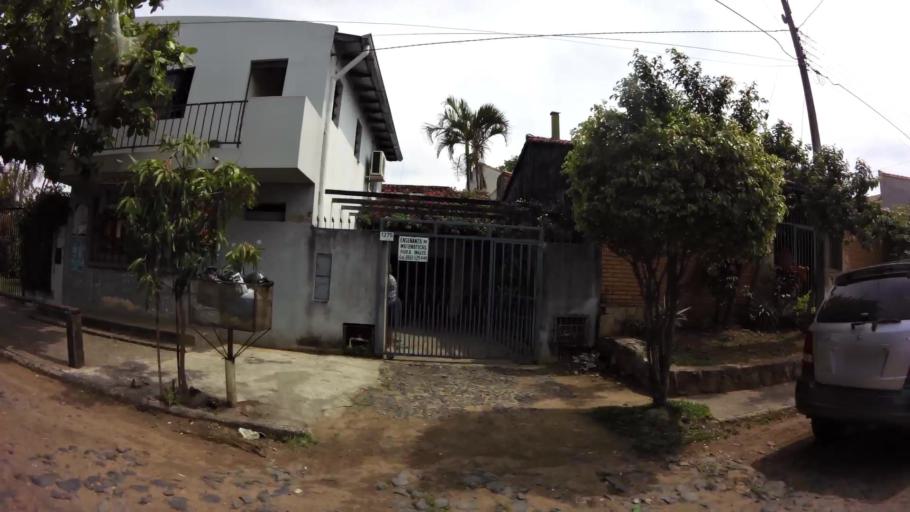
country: PY
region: Asuncion
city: Asuncion
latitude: -25.2690
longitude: -57.5873
